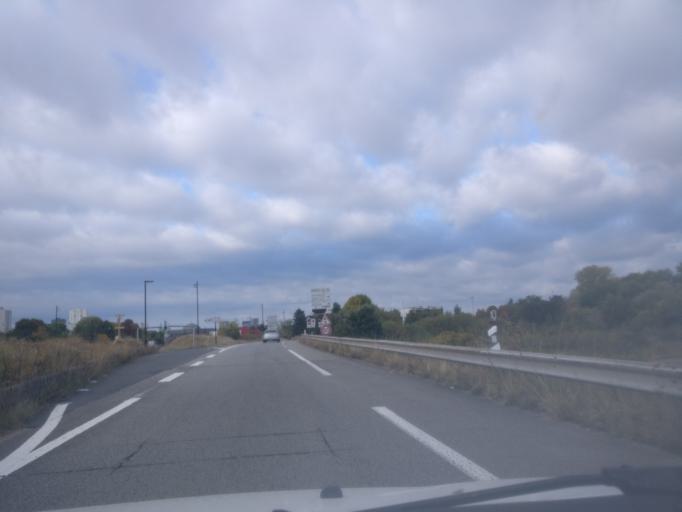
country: FR
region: Pays de la Loire
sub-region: Departement de la Loire-Atlantique
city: Saint-Sebastien-sur-Loire
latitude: 47.2208
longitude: -1.5137
